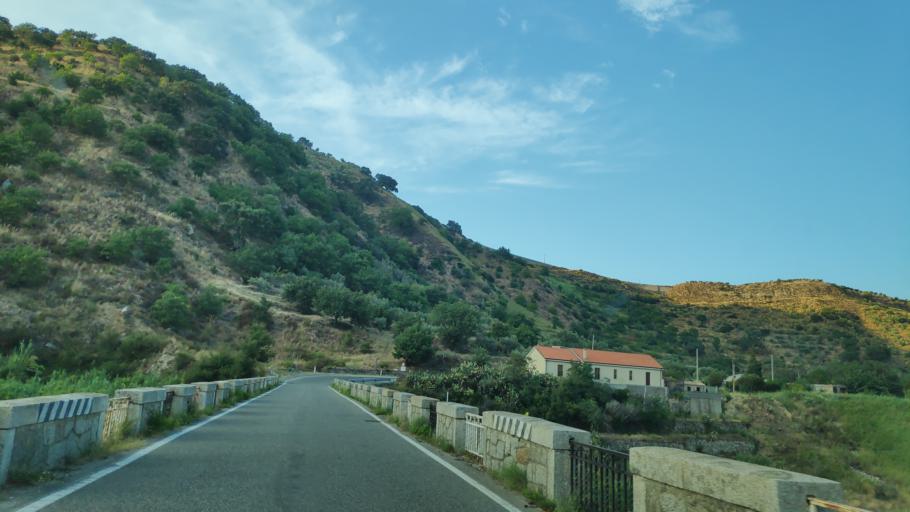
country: IT
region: Calabria
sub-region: Provincia di Catanzaro
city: Satriano
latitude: 38.6732
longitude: 16.4902
